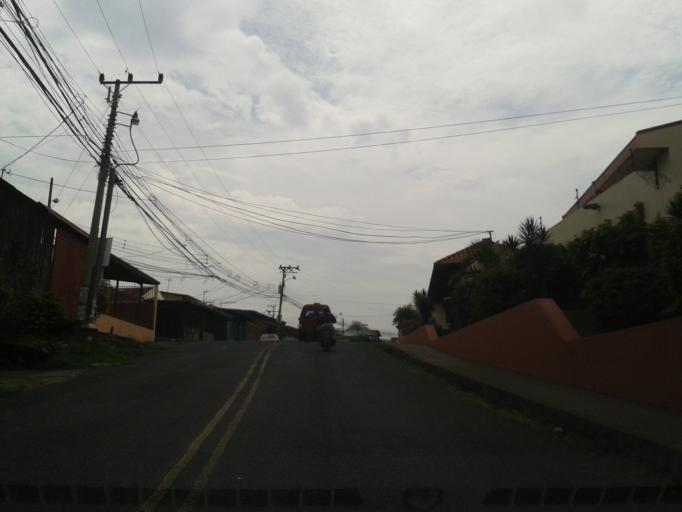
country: CR
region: Heredia
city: San Pablo
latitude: 9.9798
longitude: -84.0995
